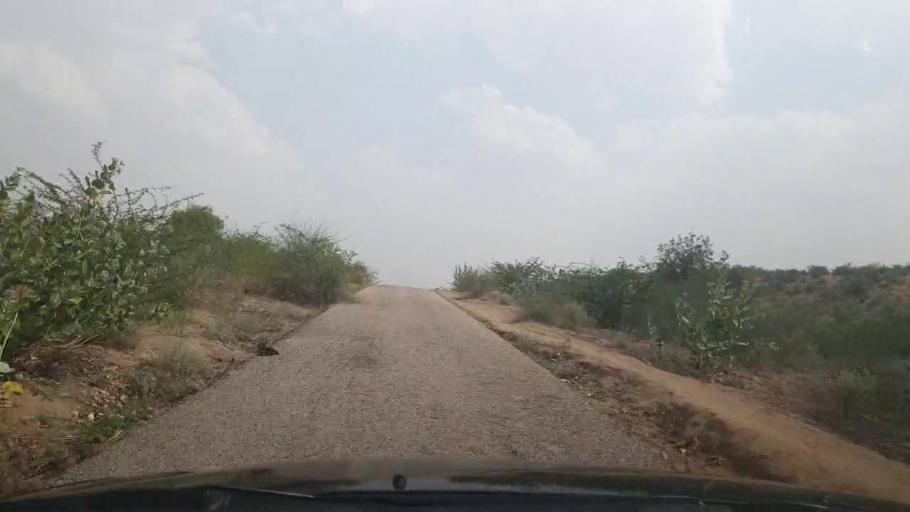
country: PK
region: Sindh
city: Islamkot
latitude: 25.0305
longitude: 70.5434
